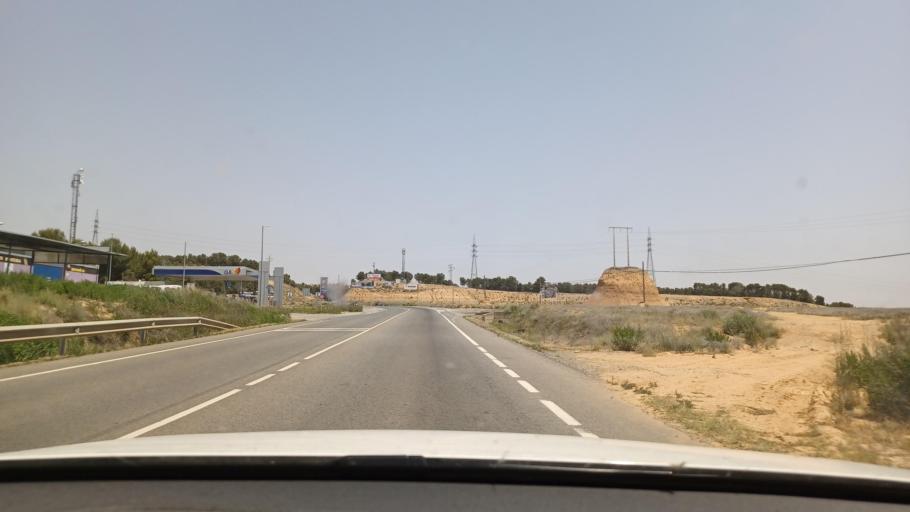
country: ES
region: Navarre
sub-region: Provincia de Navarra
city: Murchante
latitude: 42.0358
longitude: -1.6313
